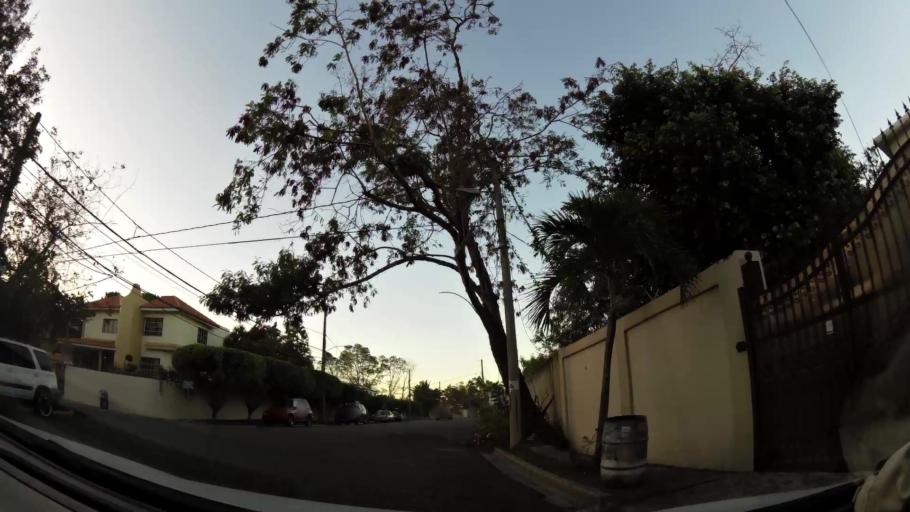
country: DO
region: Nacional
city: La Agustina
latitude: 18.5009
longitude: -69.9557
